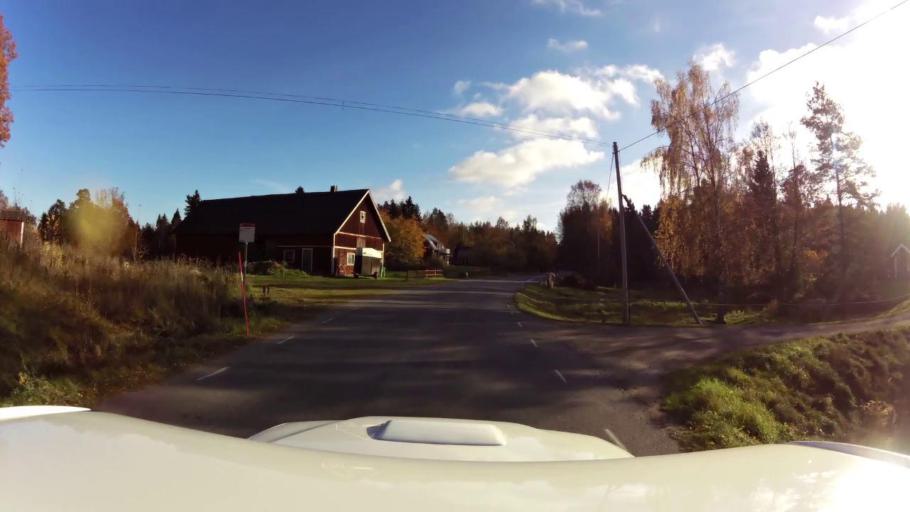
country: SE
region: OEstergoetland
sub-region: Linkopings Kommun
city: Vikingstad
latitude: 58.2682
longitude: 15.4467
